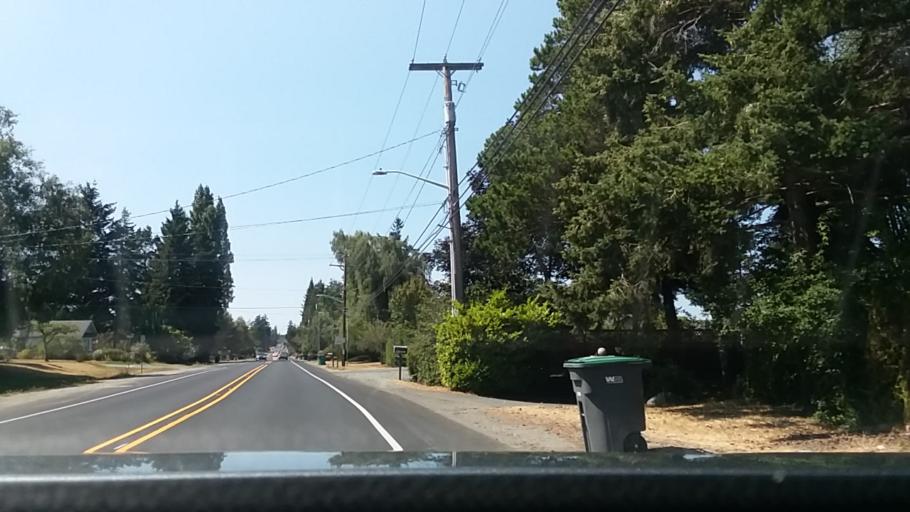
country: US
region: Washington
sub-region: Skagit County
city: Anacortes
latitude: 48.5127
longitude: -122.6364
